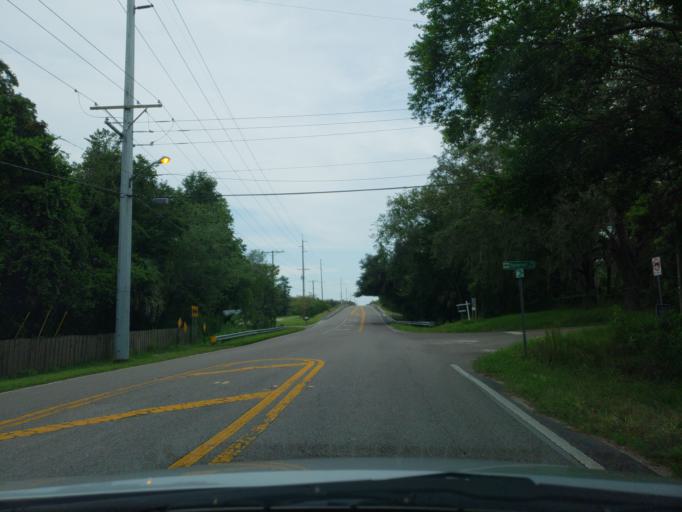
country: US
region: Florida
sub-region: Hillsborough County
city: University
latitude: 28.1100
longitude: -82.4308
